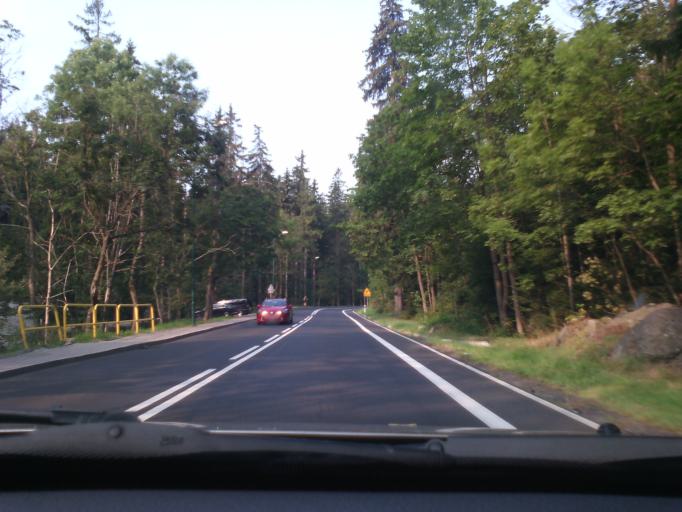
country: PL
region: Lower Silesian Voivodeship
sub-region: Powiat jeleniogorski
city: Szklarska Poreba
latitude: 50.8267
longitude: 15.5117
